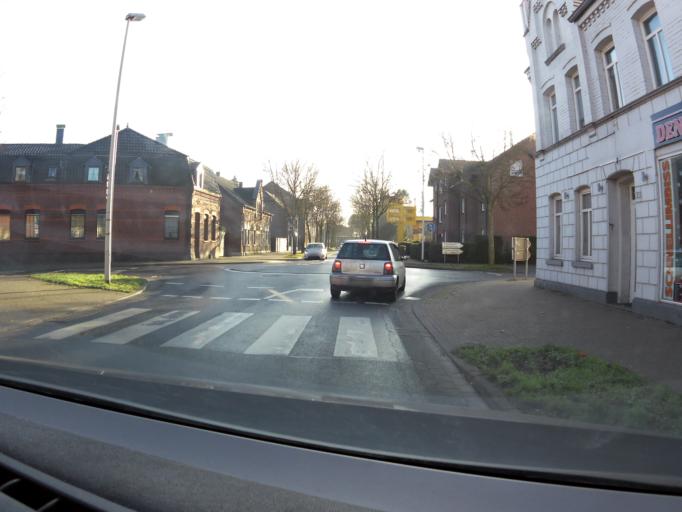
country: NL
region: Limburg
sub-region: Gemeente Venlo
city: Venlo
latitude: 51.3160
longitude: 6.2014
